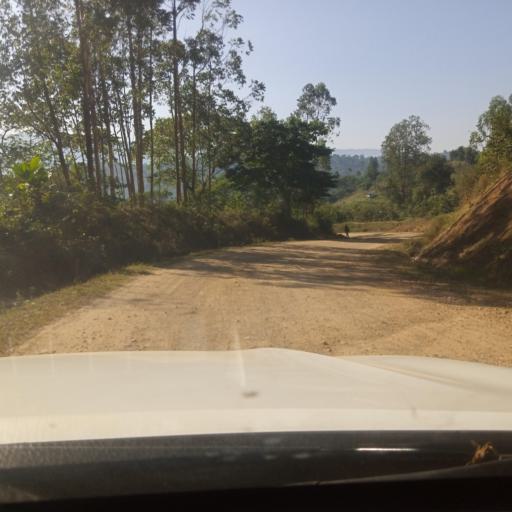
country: ET
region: Southern Nations, Nationalities, and People's Region
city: Mizan Teferi
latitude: 7.0247
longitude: 35.5537
